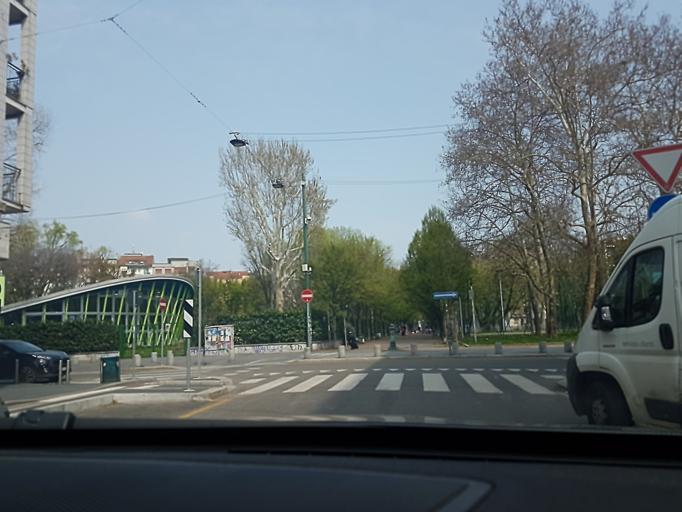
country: IT
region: Lombardy
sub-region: Citta metropolitana di Milano
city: Milano
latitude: 45.4577
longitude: 9.1649
